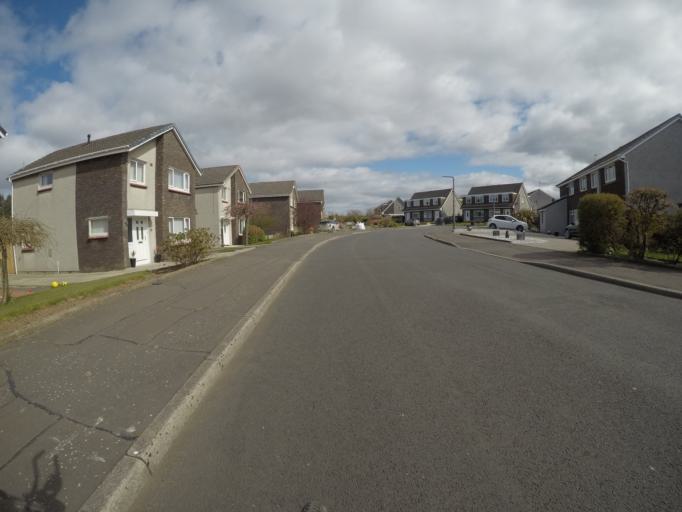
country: GB
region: Scotland
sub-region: South Ayrshire
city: Troon
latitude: 55.5668
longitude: -4.6415
